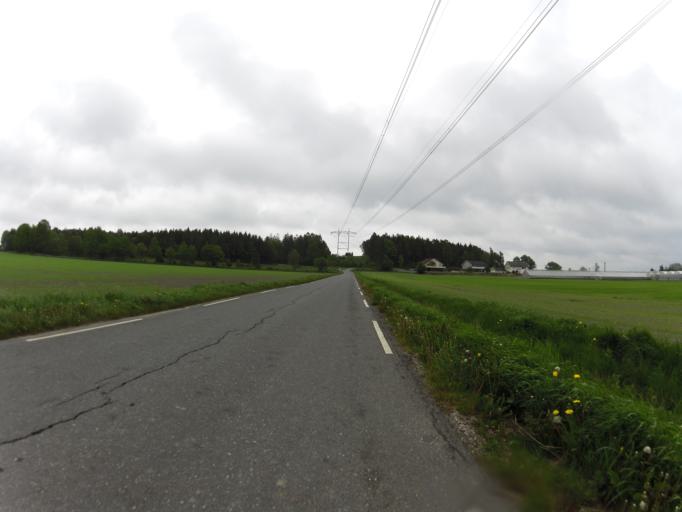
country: NO
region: Ostfold
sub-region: Rygge
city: Ryggebyen
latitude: 59.3569
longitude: 10.7454
